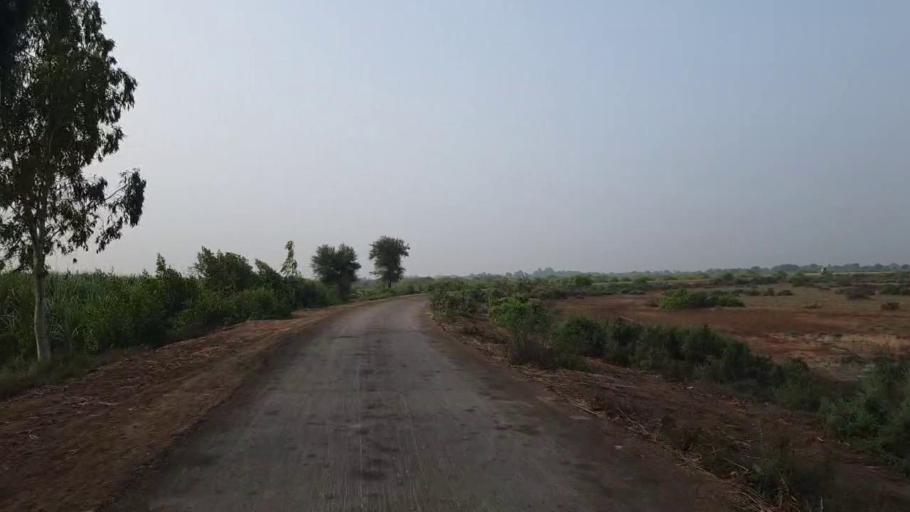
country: PK
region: Sindh
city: Tando Muhammad Khan
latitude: 25.1531
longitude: 68.6084
